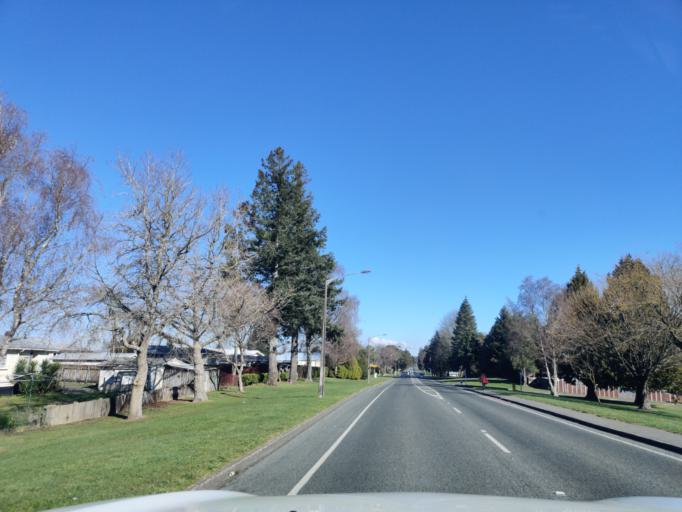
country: NZ
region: Waikato
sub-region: South Waikato District
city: Tokoroa
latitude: -38.2274
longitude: 175.8712
